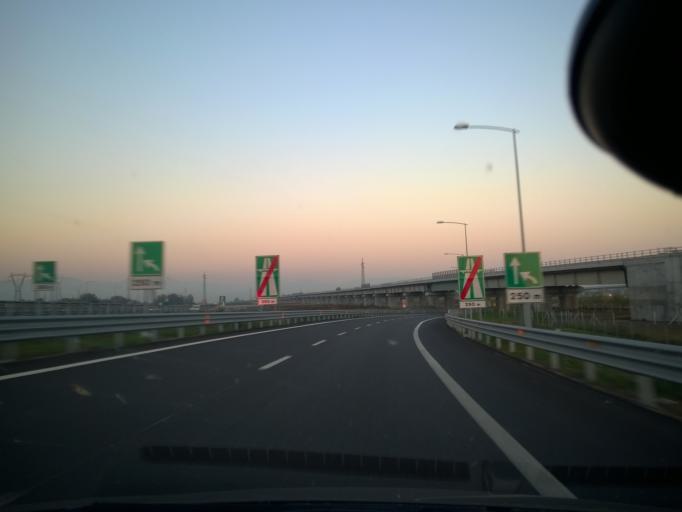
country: IT
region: Lombardy
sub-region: Provincia di Brescia
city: Lodetto
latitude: 45.5294
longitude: 10.0485
